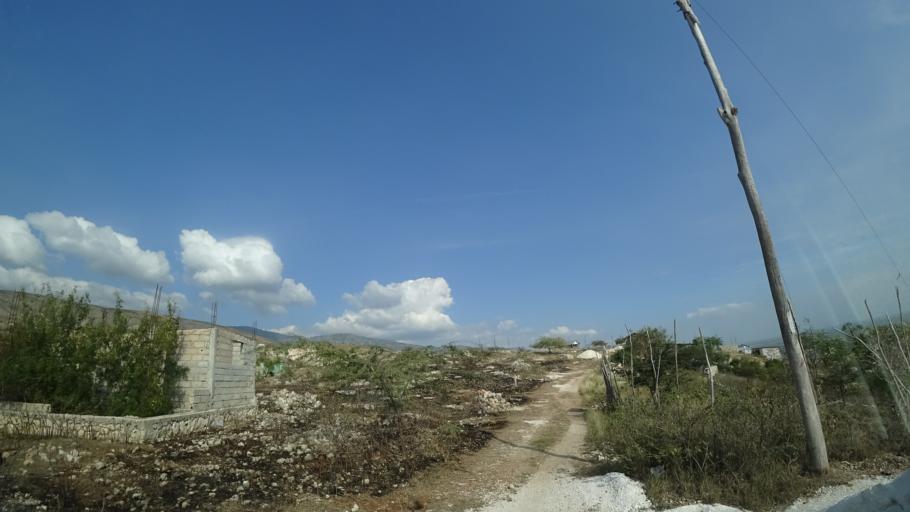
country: HT
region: Ouest
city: Croix des Bouquets
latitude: 18.6661
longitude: -72.2768
